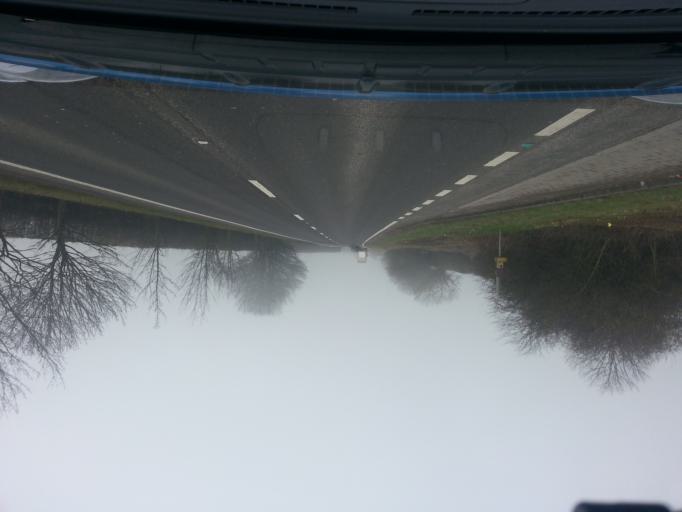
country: GB
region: England
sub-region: Oxfordshire
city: Faringdon
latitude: 51.6588
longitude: -1.5651
